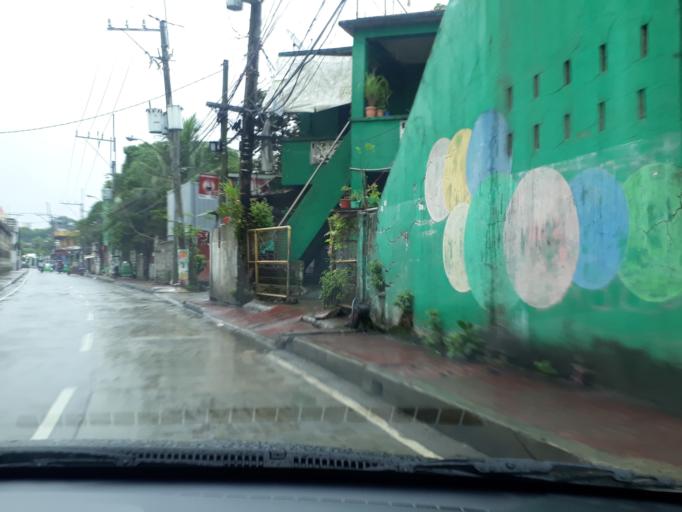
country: PH
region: Calabarzon
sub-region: Province of Rizal
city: Valenzuela
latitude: 14.7123
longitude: 120.9850
